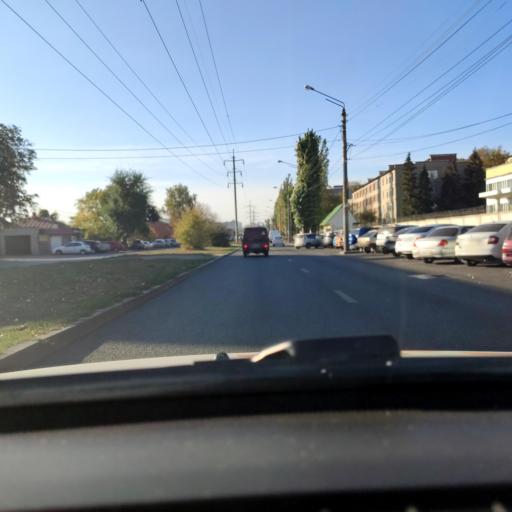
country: RU
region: Voronezj
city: Voronezh
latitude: 51.6339
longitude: 39.1776
